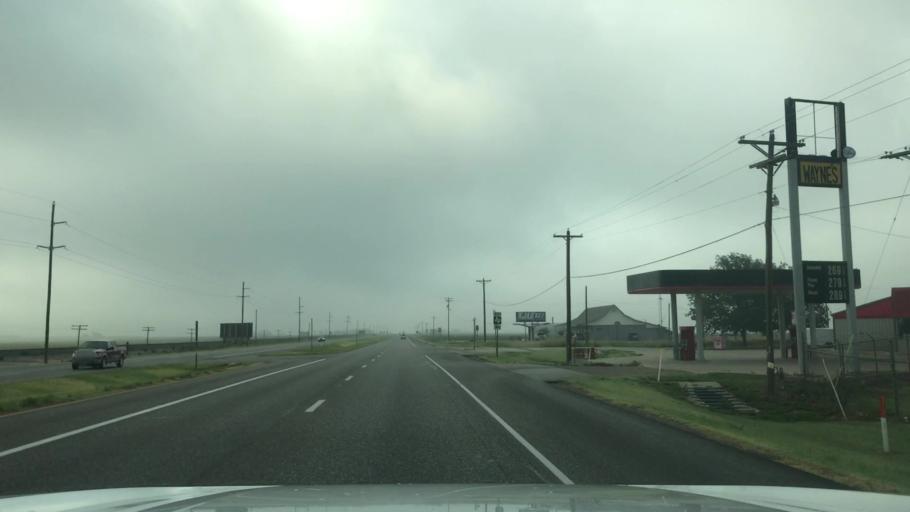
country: US
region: Texas
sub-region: Lubbock County
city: Ransom Canyon
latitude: 33.4925
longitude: -101.7286
